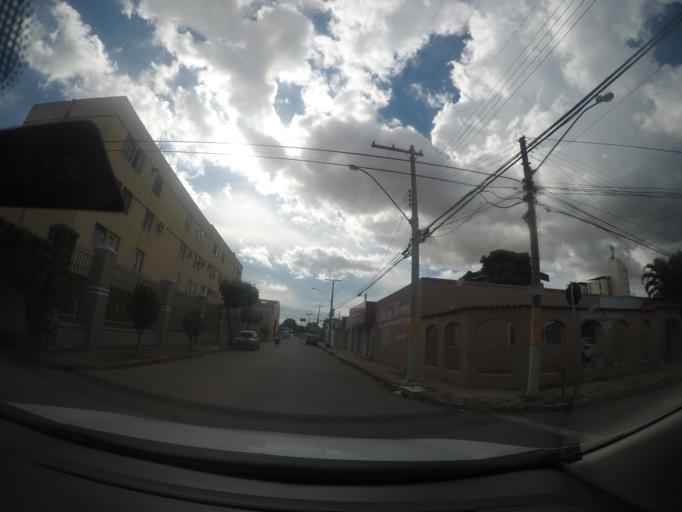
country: BR
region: Goias
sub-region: Goiania
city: Goiania
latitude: -16.6740
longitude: -49.3046
